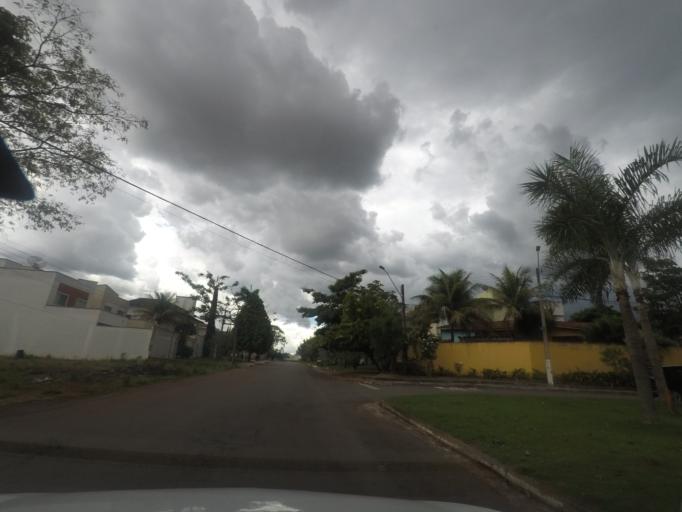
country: BR
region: Goias
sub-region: Goiania
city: Goiania
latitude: -16.6437
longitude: -49.2269
